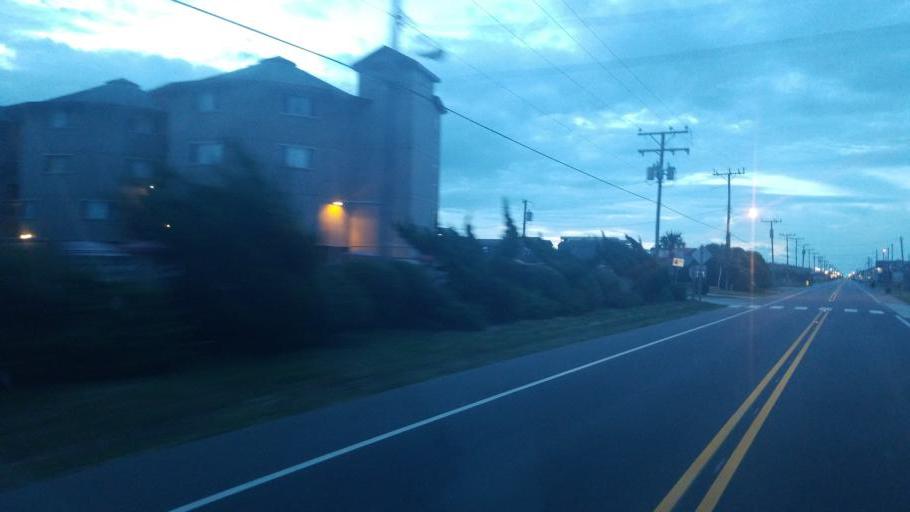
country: US
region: North Carolina
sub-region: Dare County
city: Kill Devil Hills
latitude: 36.0063
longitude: -75.6527
